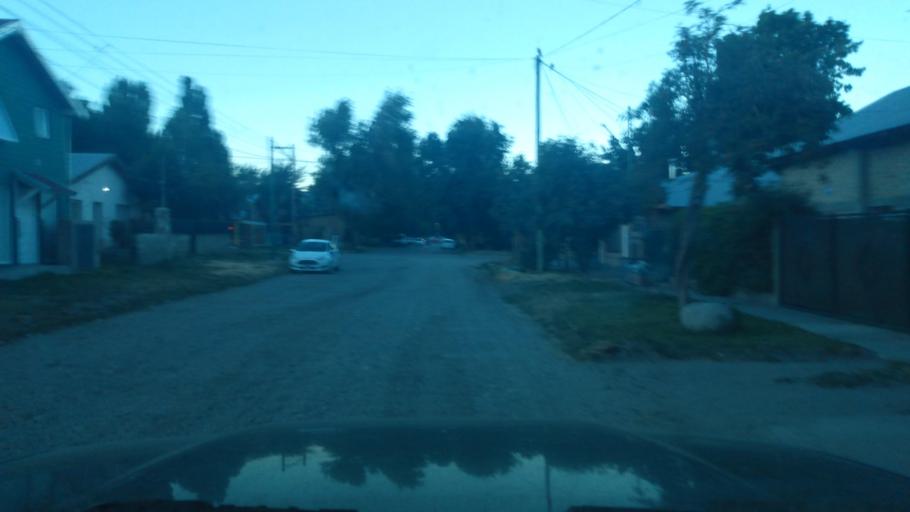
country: AR
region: Neuquen
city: Junin de los Andes
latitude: -39.9525
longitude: -71.0736
